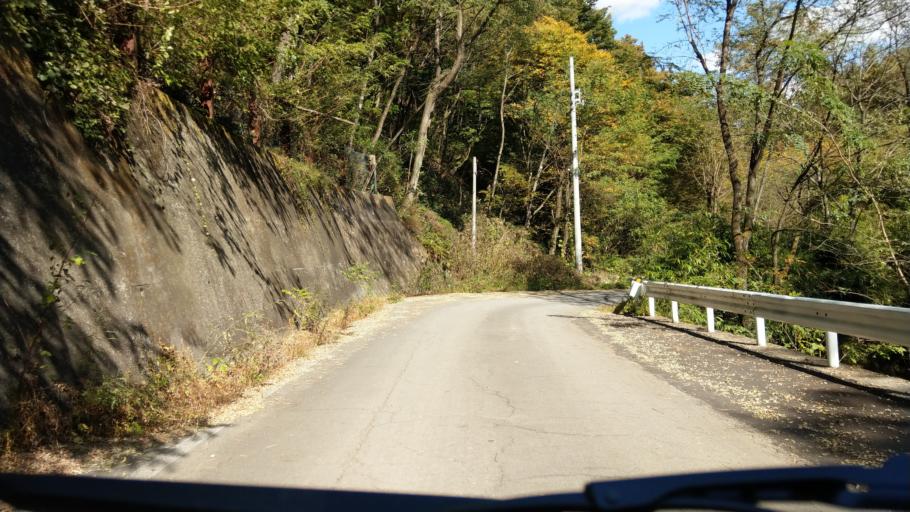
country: JP
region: Nagano
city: Komoro
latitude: 36.3551
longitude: 138.4024
